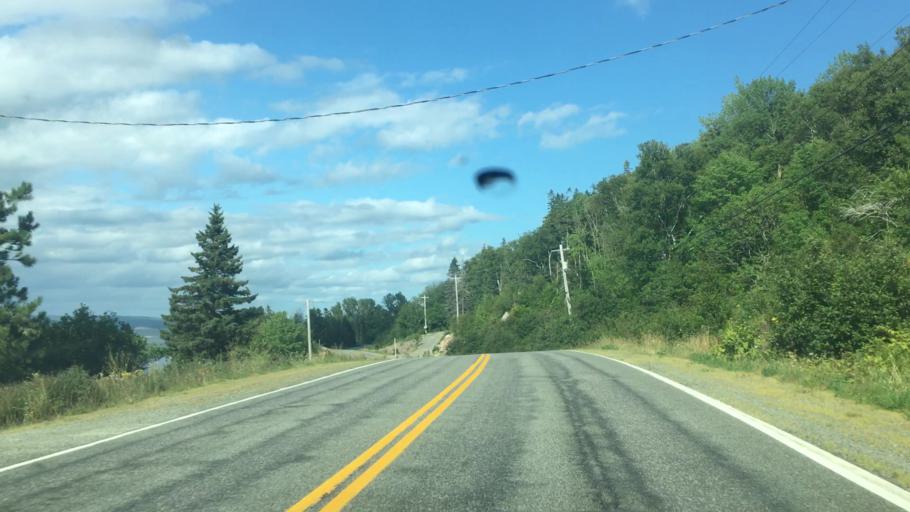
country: CA
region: Nova Scotia
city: Sydney
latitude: 45.8716
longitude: -60.6070
